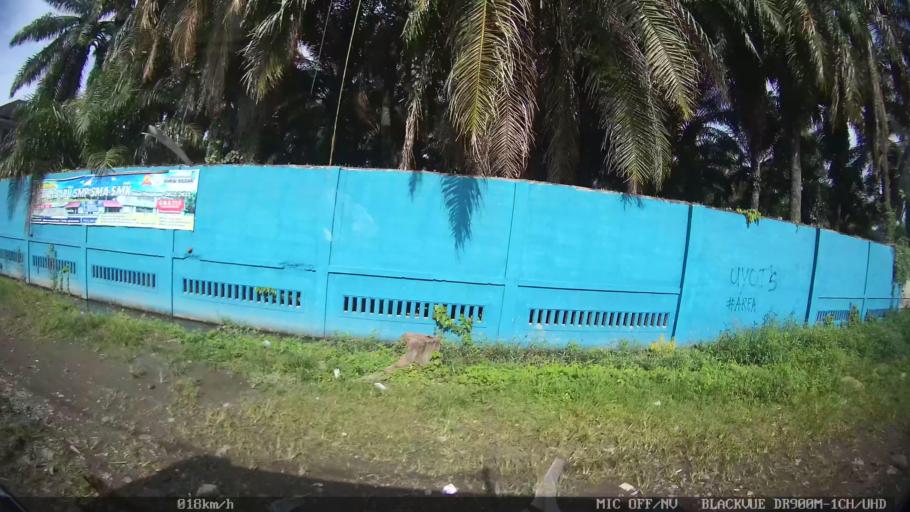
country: ID
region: North Sumatra
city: Medan
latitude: 3.6191
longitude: 98.6602
